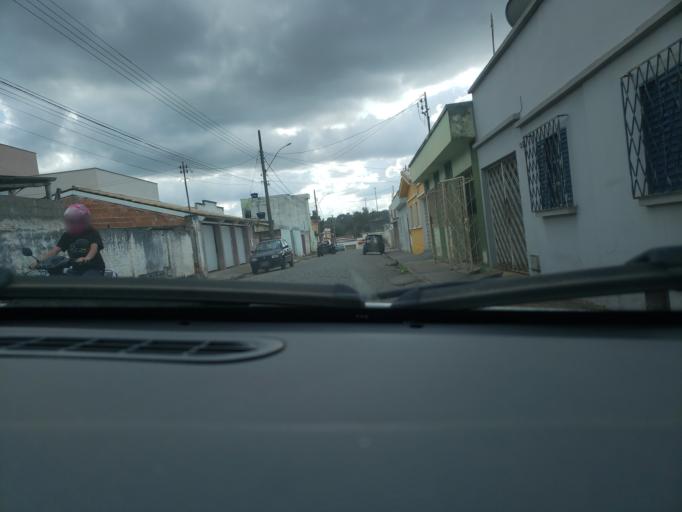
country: BR
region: Minas Gerais
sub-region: Campo Belo
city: Campo Belo
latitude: -20.8988
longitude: -45.2681
